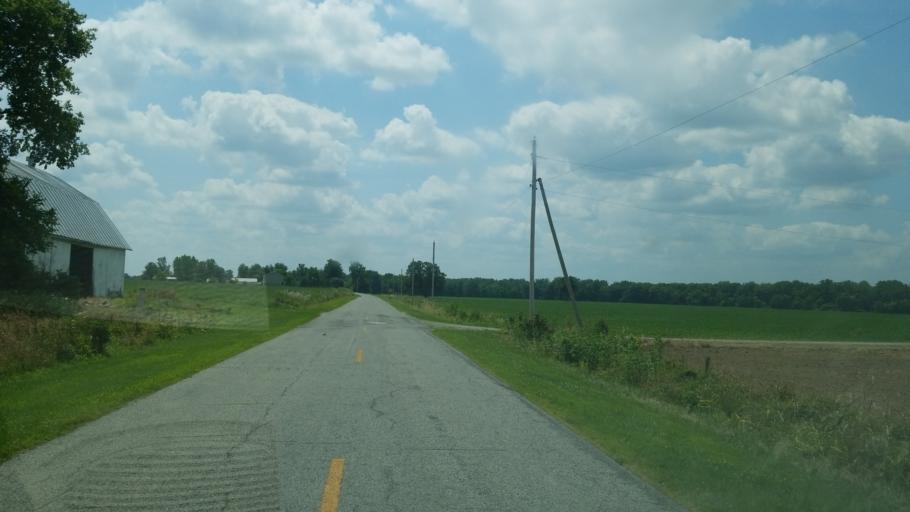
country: US
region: Ohio
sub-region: Henry County
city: Napoleon
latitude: 41.3650
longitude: -84.1429
